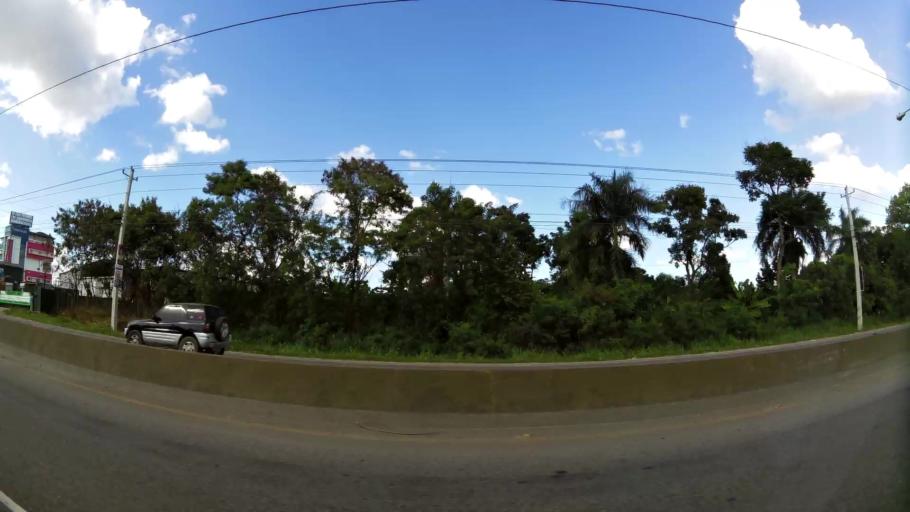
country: DO
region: Santo Domingo
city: Santo Domingo Oeste
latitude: 18.5400
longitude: -70.0314
